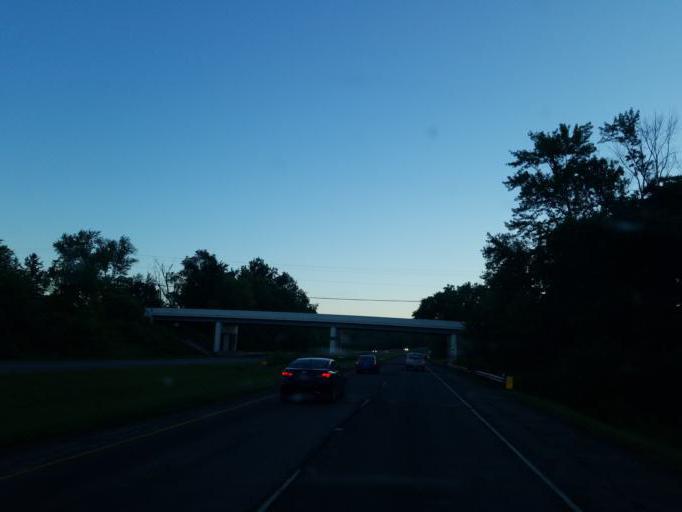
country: US
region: Ohio
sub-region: Summit County
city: Norton
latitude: 41.0252
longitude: -81.6653
